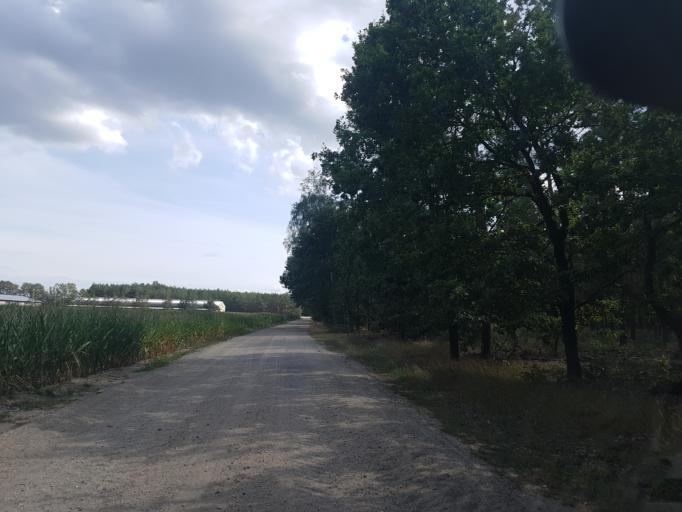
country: DE
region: Brandenburg
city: Doberlug-Kirchhain
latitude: 51.6602
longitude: 13.5097
